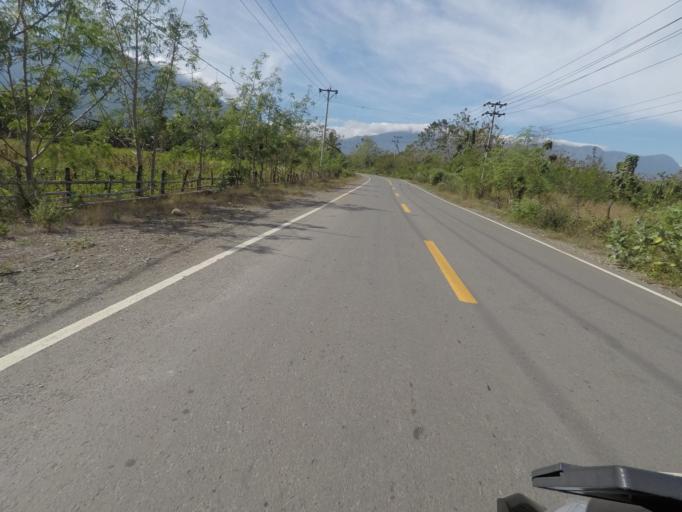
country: TL
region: Bobonaro
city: Maliana
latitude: -8.9465
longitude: 125.2049
